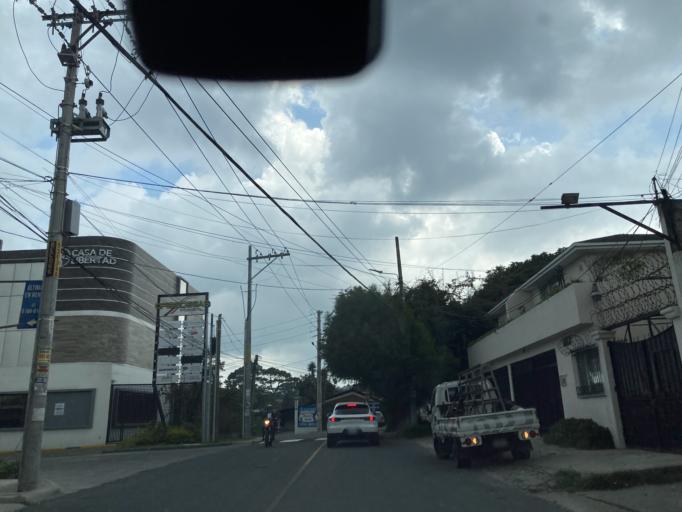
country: GT
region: Guatemala
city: Santa Catarina Pinula
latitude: 14.5584
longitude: -90.4600
